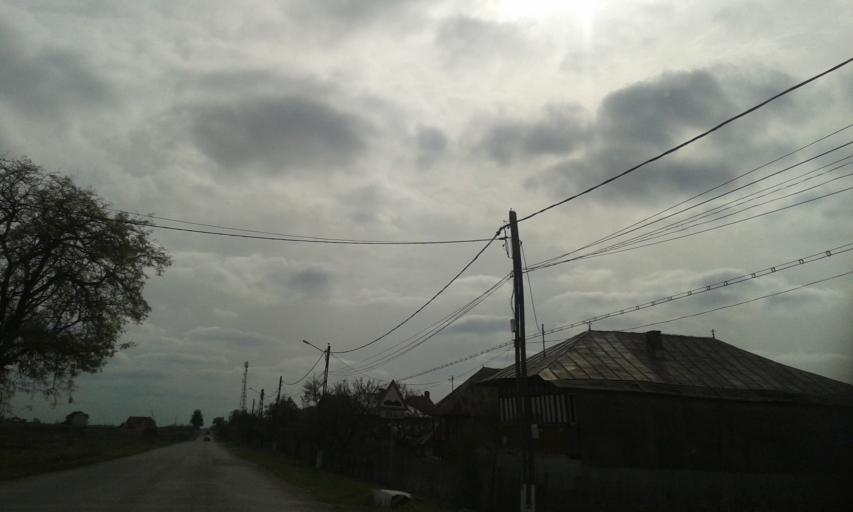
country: RO
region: Gorj
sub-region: Comuna Targu Carbunesti
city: Pojogeni
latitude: 44.9939
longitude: 23.4941
